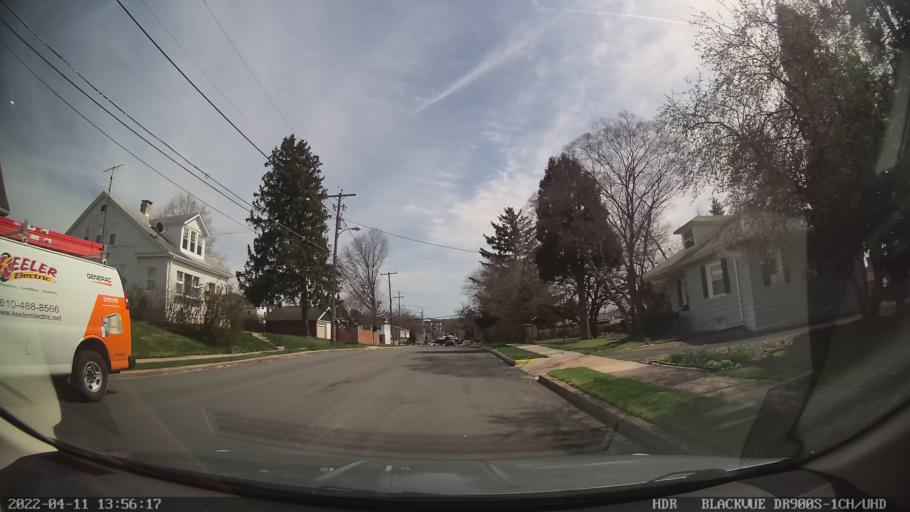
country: US
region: Pennsylvania
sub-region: Berks County
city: Laureldale
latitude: 40.3911
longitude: -75.9111
